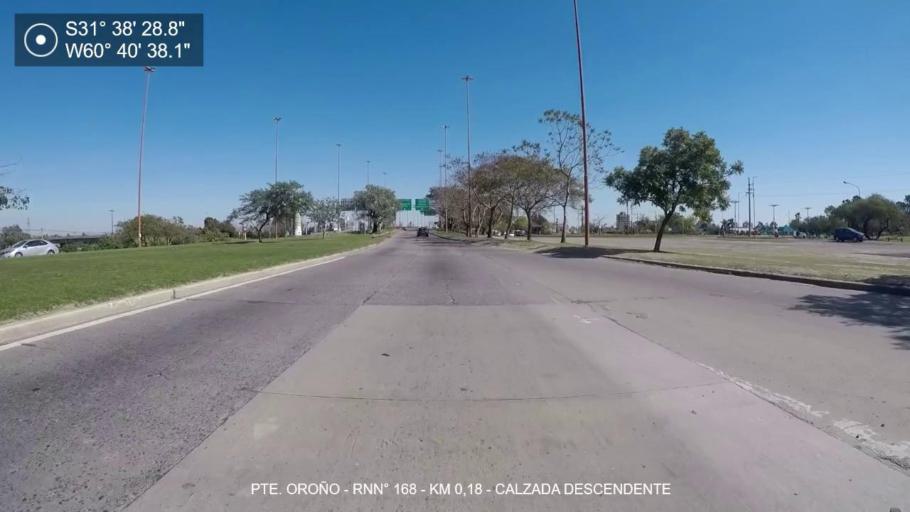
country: AR
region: Santa Fe
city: Santa Fe de la Vera Cruz
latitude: -31.6414
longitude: -60.6767
